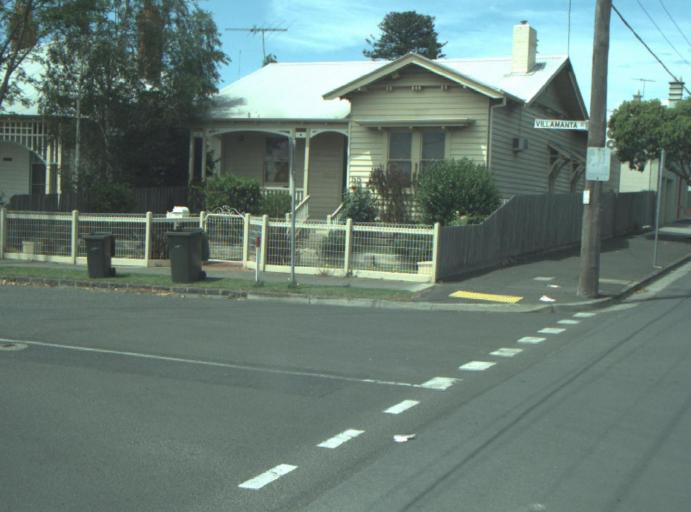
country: AU
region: Victoria
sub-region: Greater Geelong
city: Geelong West
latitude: -38.1457
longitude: 144.3474
